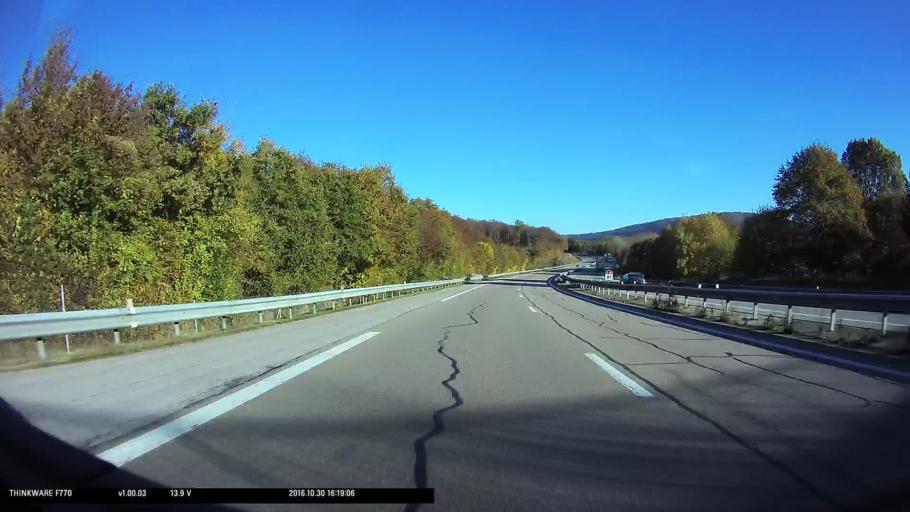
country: FR
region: Franche-Comte
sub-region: Departement du Doubs
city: Clerval
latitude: 47.4078
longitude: 6.4829
